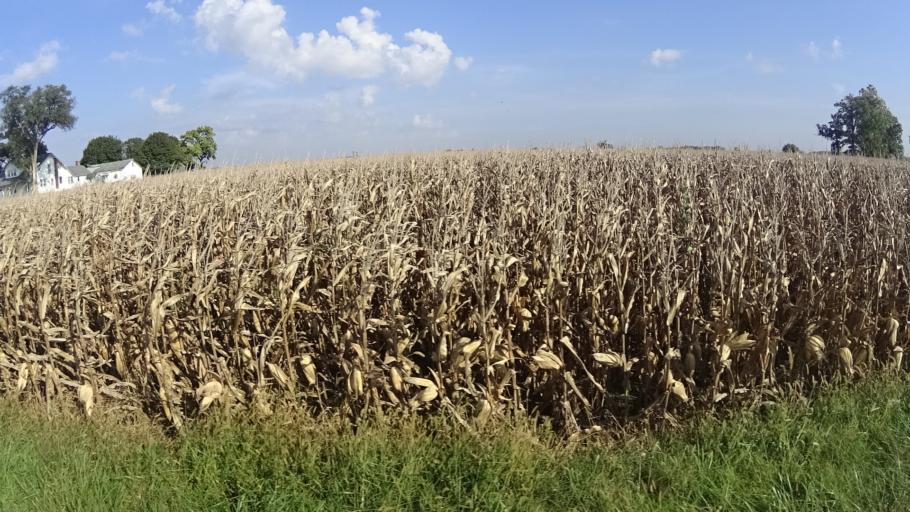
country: US
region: Indiana
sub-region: Madison County
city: Lapel
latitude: 40.0456
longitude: -85.8356
